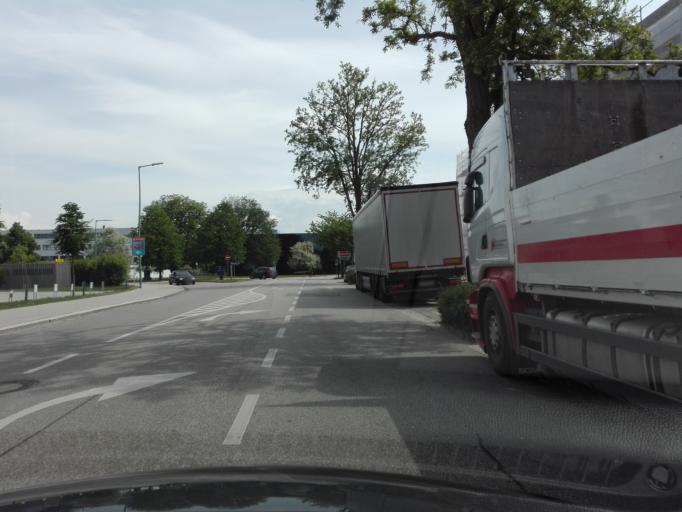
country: AT
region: Upper Austria
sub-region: Wels-Land
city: Thalheim bei Wels
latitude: 48.1542
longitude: 14.0075
